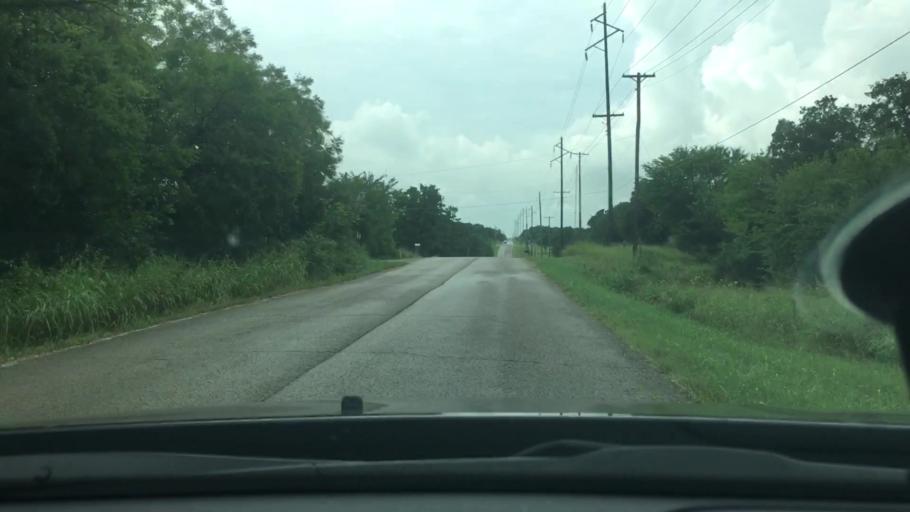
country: US
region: Oklahoma
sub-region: Carter County
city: Healdton
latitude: 34.2210
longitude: -97.4923
